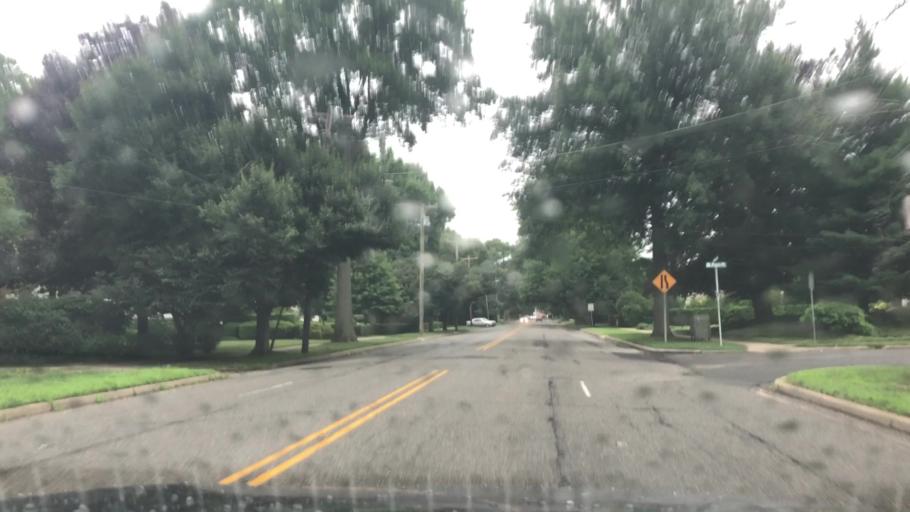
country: US
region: New York
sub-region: Nassau County
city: Garden City
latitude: 40.7131
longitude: -73.6371
